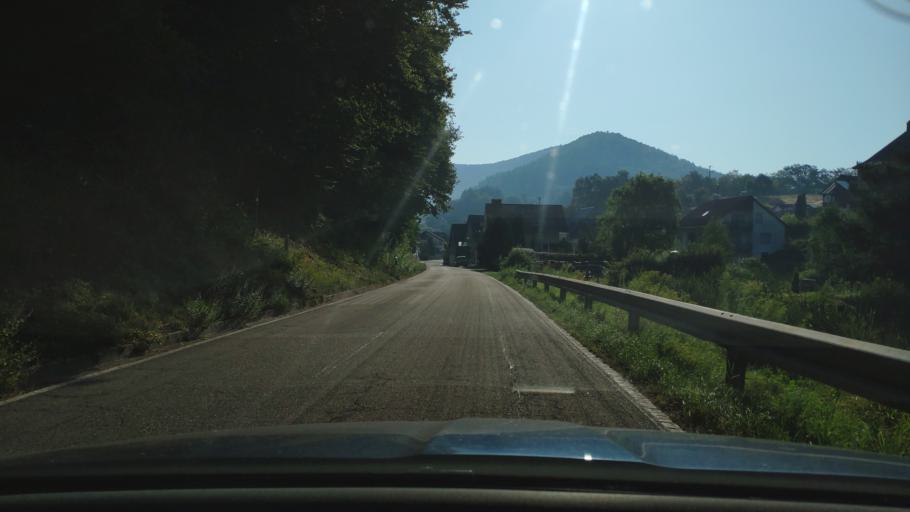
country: DE
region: Rheinland-Pfalz
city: Hirschthal
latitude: 49.0608
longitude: 7.7417
